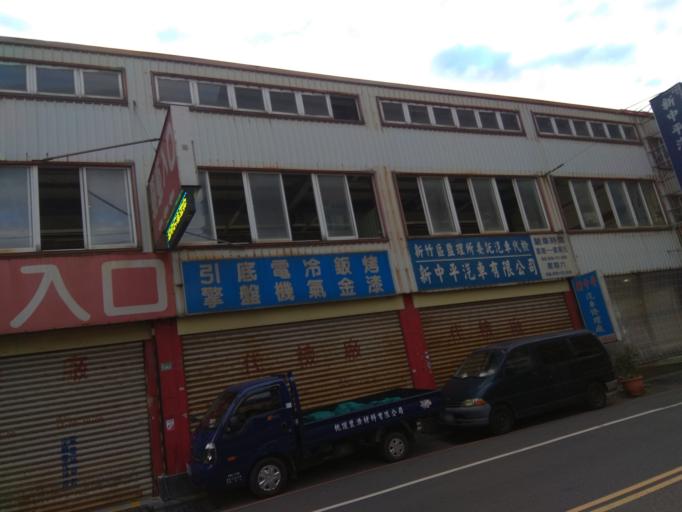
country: TW
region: Taiwan
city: Taoyuan City
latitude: 24.9953
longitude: 121.3075
